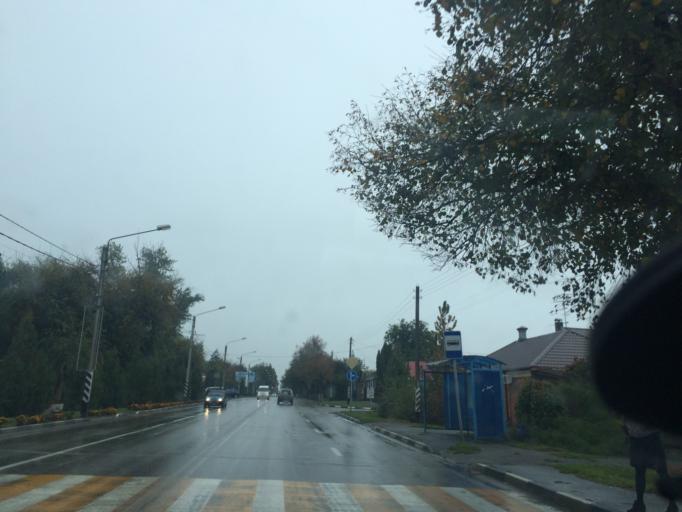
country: RU
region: Rostov
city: Azov
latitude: 47.1014
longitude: 39.4383
